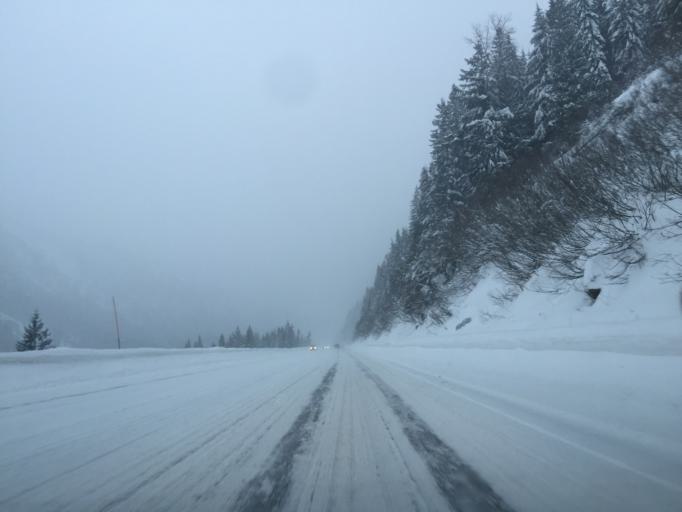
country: US
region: Washington
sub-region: Chelan County
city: Leavenworth
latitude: 47.7473
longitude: -121.1145
